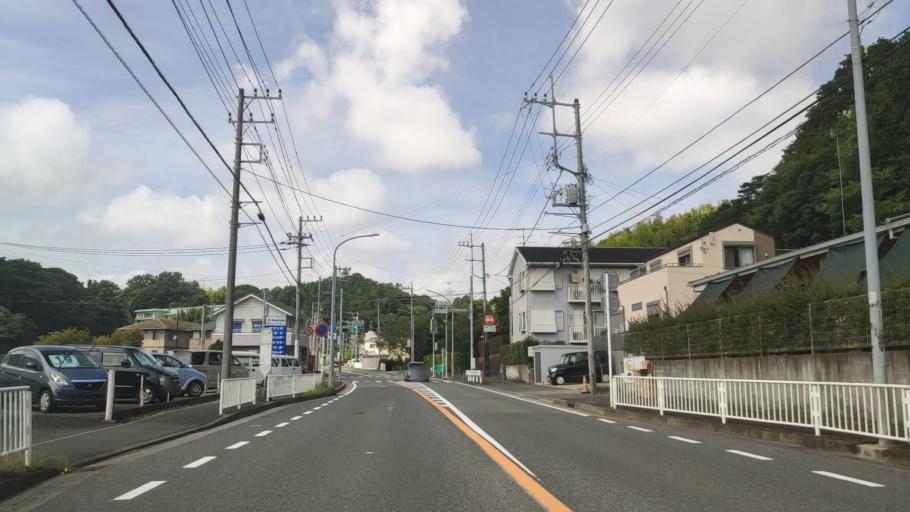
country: JP
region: Kanagawa
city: Minami-rinkan
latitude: 35.4320
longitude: 139.5325
